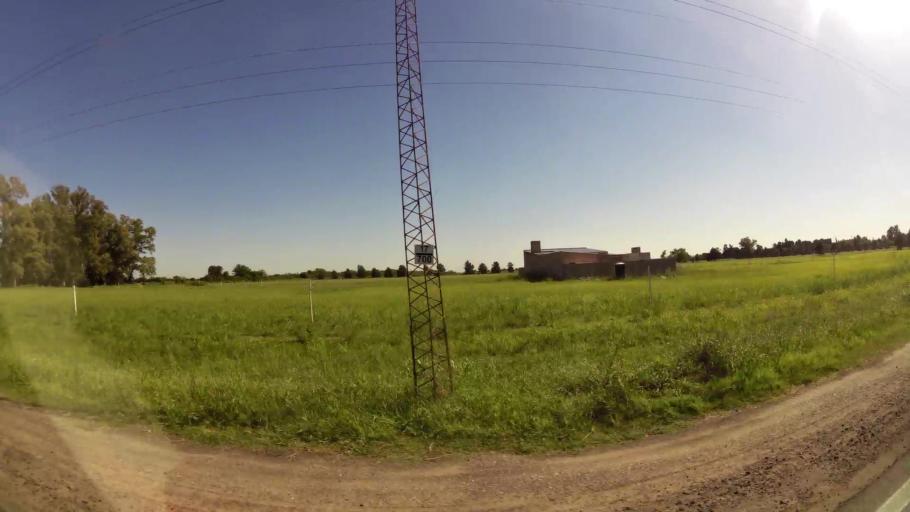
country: AR
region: Santa Fe
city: Esperanza
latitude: -31.4505
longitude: -60.8983
